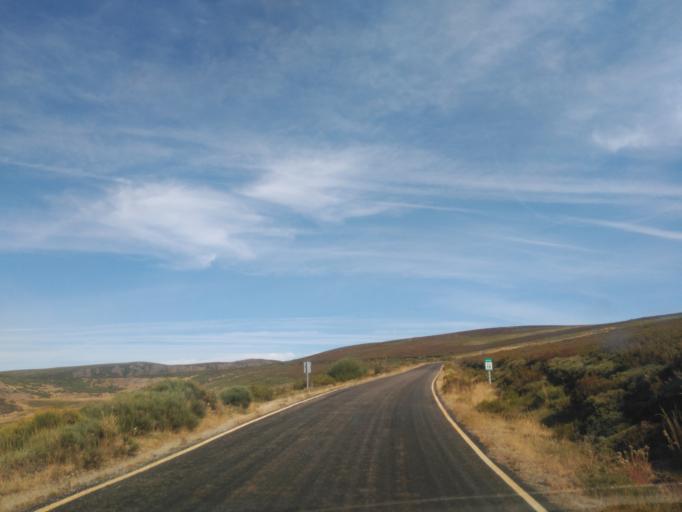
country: ES
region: Castille and Leon
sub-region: Provincia de Zamora
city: Trefacio
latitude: 42.1575
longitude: -6.7242
